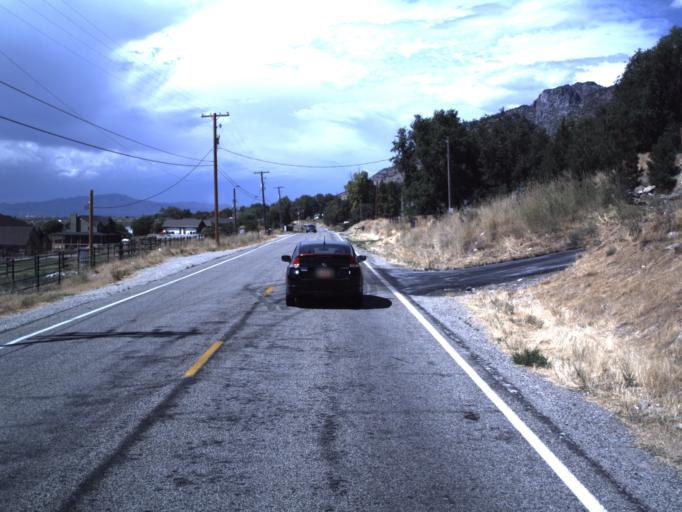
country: US
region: Utah
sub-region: Box Elder County
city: Brigham City
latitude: 41.5724
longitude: -112.0301
